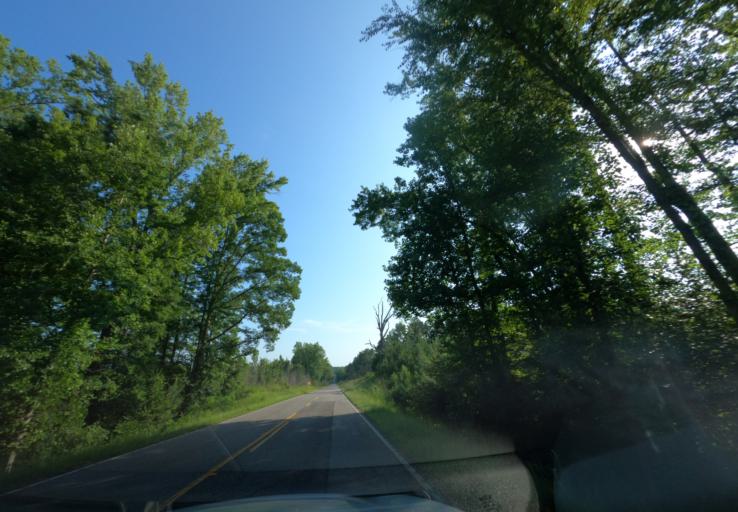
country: US
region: South Carolina
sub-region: Edgefield County
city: Edgefield
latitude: 33.7468
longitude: -81.9599
